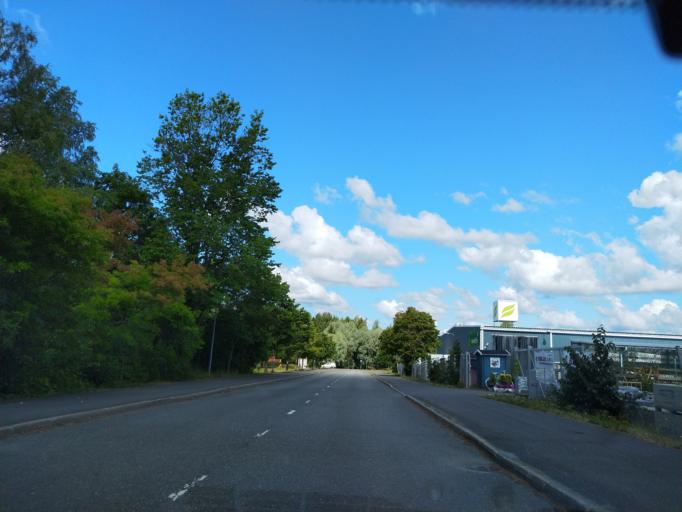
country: FI
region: Satakunta
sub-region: Pori
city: Huittinen
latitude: 61.1753
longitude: 22.6955
